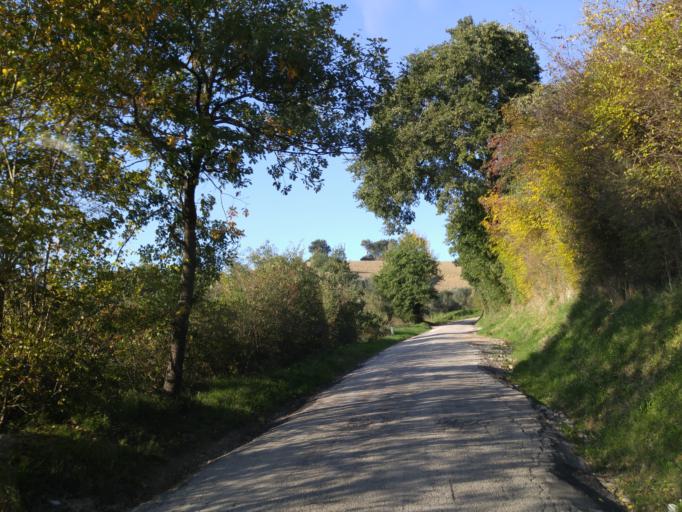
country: IT
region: The Marches
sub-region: Provincia di Pesaro e Urbino
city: Fossombrone
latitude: 43.7055
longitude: 12.8131
